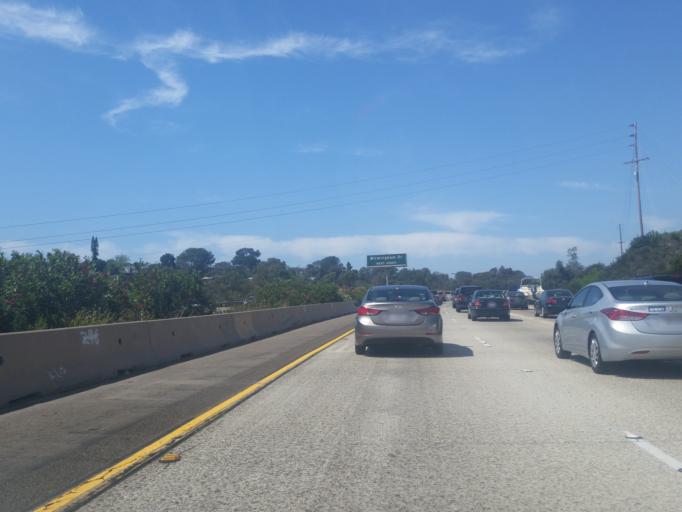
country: US
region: California
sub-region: San Diego County
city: Solana Beach
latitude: 33.0174
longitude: -117.2718
